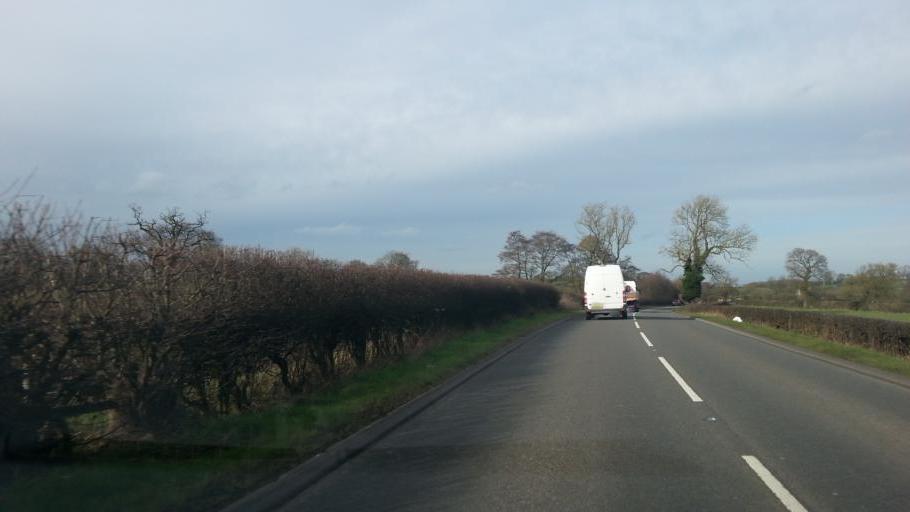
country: GB
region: England
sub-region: Staffordshire
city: Uttoxeter
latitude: 52.8736
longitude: -1.9393
